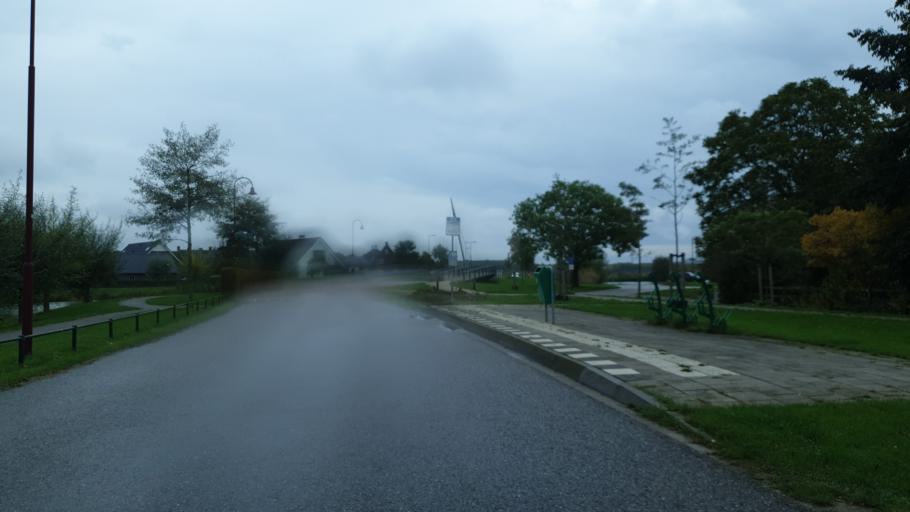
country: NL
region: Gelderland
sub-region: Gemeente Beuningen
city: Beuningen
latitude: 51.8484
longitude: 5.7710
